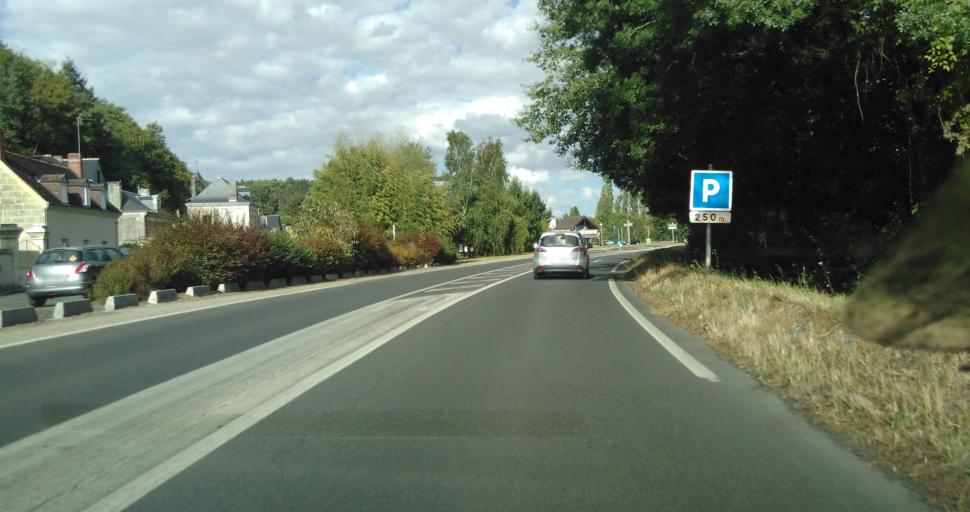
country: FR
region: Centre
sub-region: Departement d'Indre-et-Loire
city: Saint-Etienne-de-Chigny
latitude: 47.3687
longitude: 0.5133
